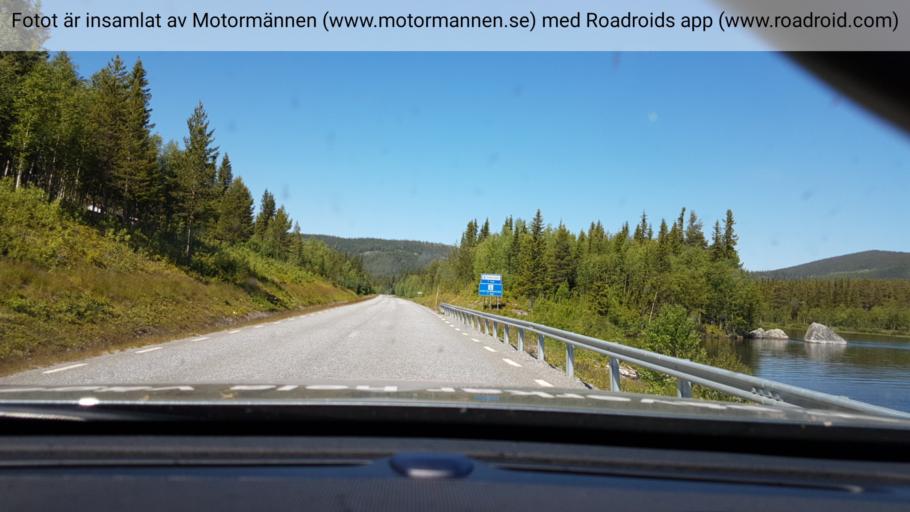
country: SE
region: Vaesterbotten
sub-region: Vilhelmina Kommun
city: Sjoberg
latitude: 64.9275
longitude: 15.8639
